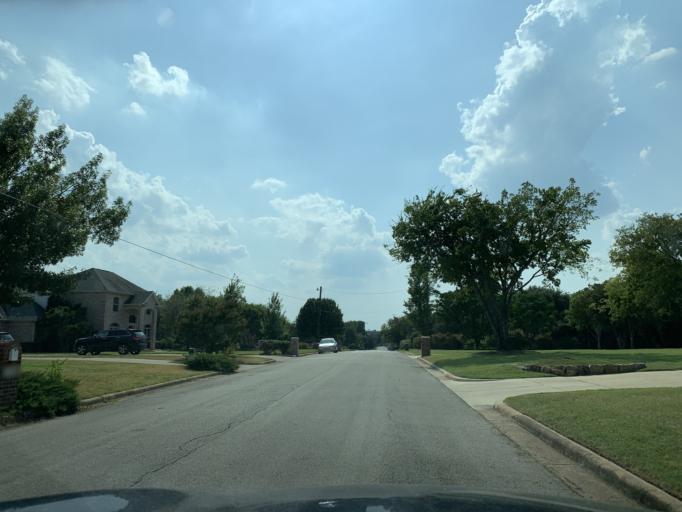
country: US
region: Texas
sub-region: Tarrant County
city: Richland Hills
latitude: 32.8113
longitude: -97.2249
